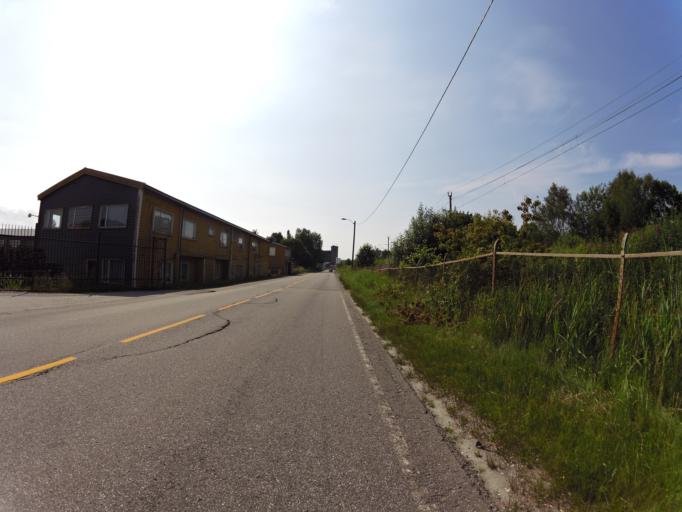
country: NO
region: Ostfold
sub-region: Sarpsborg
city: Sarpsborg
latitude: 59.2645
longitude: 11.0439
